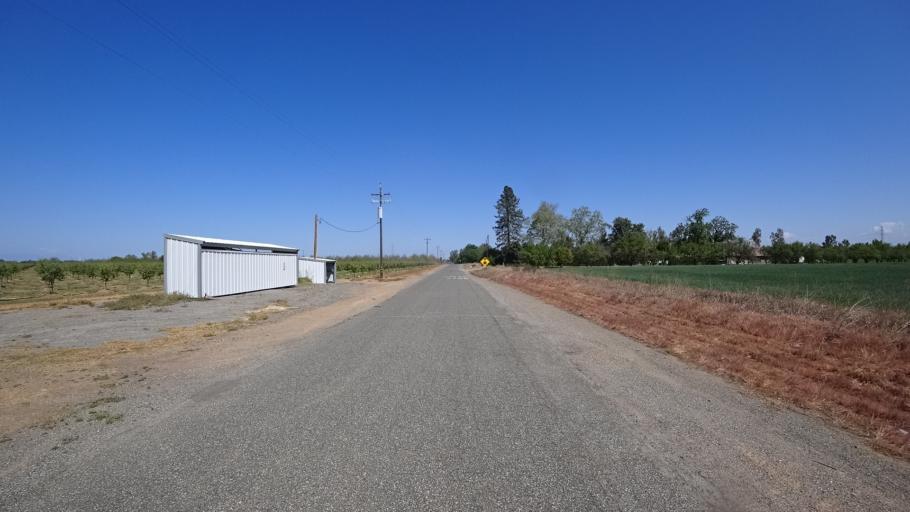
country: US
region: California
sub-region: Glenn County
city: Orland
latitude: 39.7846
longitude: -122.1597
